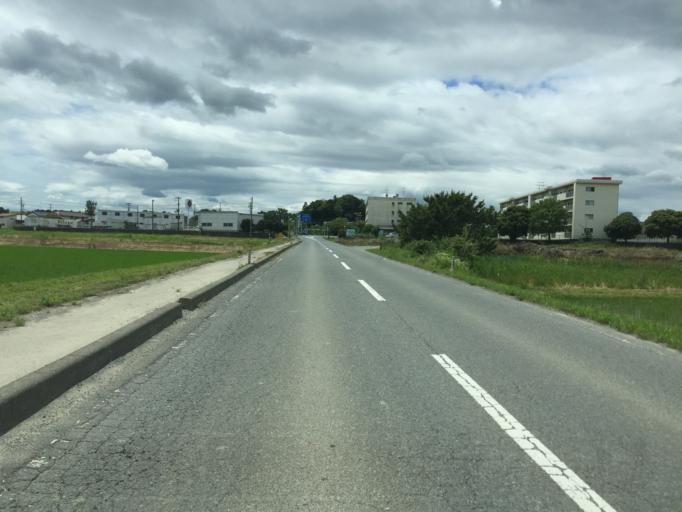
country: JP
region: Fukushima
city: Namie
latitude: 37.6219
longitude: 140.9999
